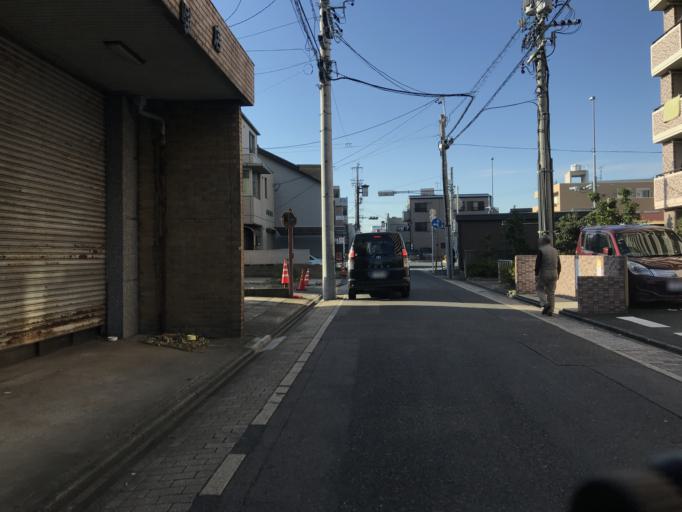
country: JP
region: Aichi
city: Nagoya-shi
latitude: 35.1893
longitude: 136.8772
